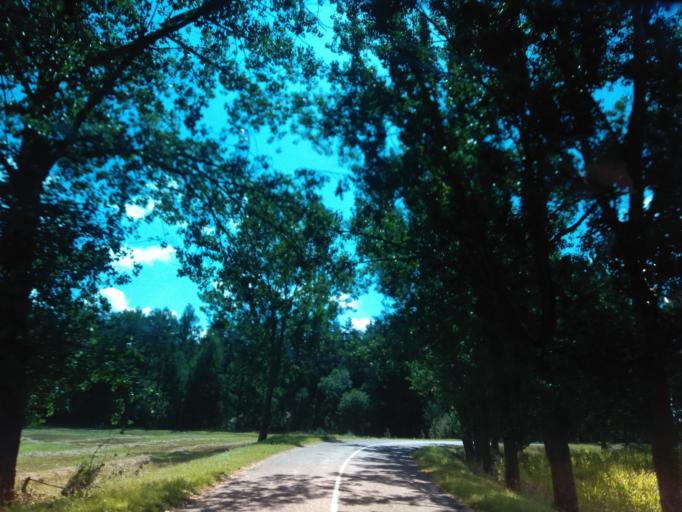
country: BY
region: Minsk
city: Kapyl'
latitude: 53.2750
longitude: 27.2306
